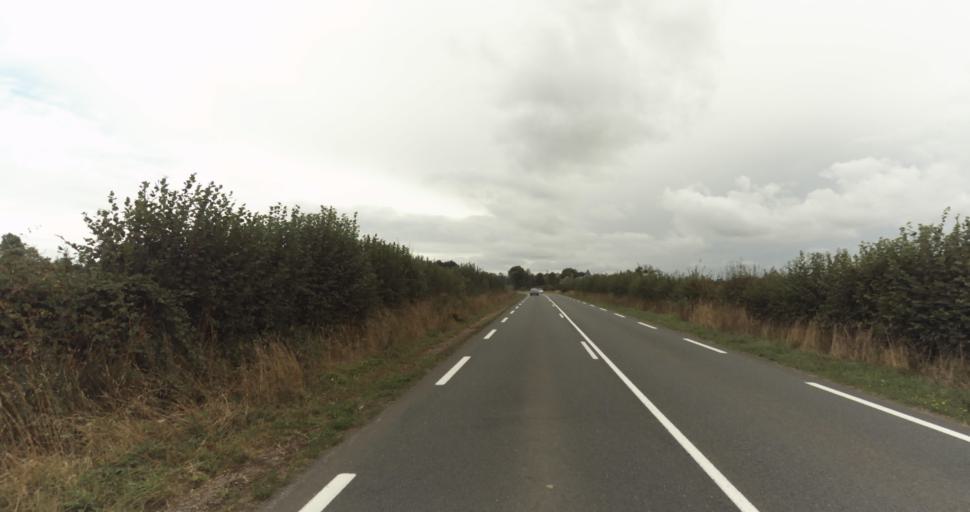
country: FR
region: Lower Normandy
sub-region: Departement de l'Orne
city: Vimoutiers
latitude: 48.8694
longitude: 0.2533
